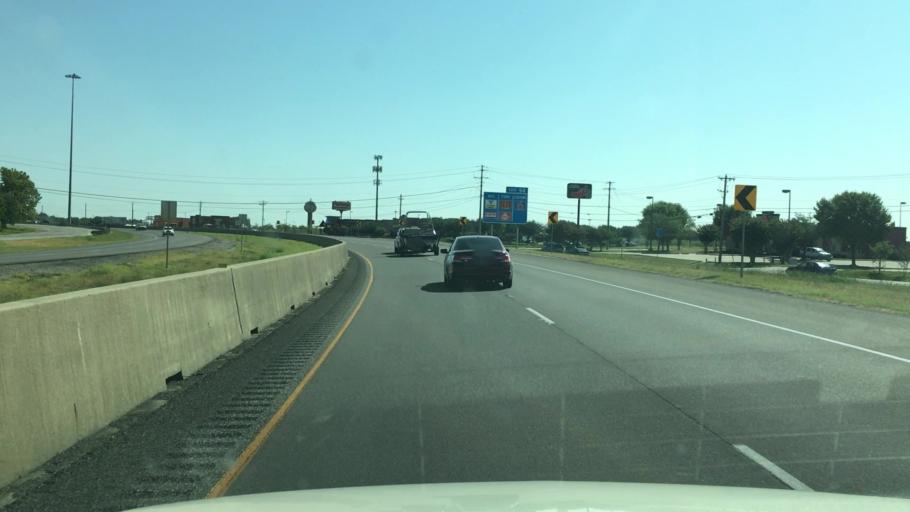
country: US
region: Texas
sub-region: Hunt County
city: Greenville
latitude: 33.0977
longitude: -96.1068
